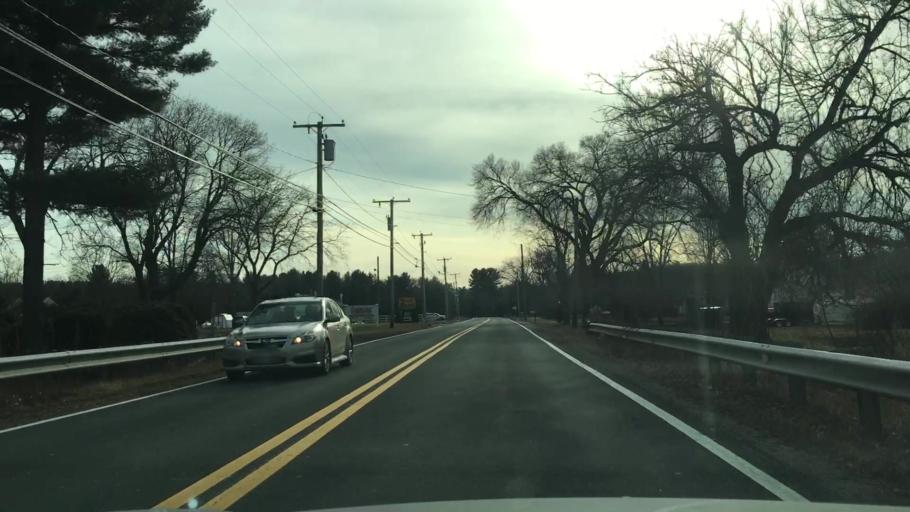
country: US
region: Massachusetts
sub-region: Hampden County
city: Southwick
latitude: 42.0866
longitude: -72.7649
